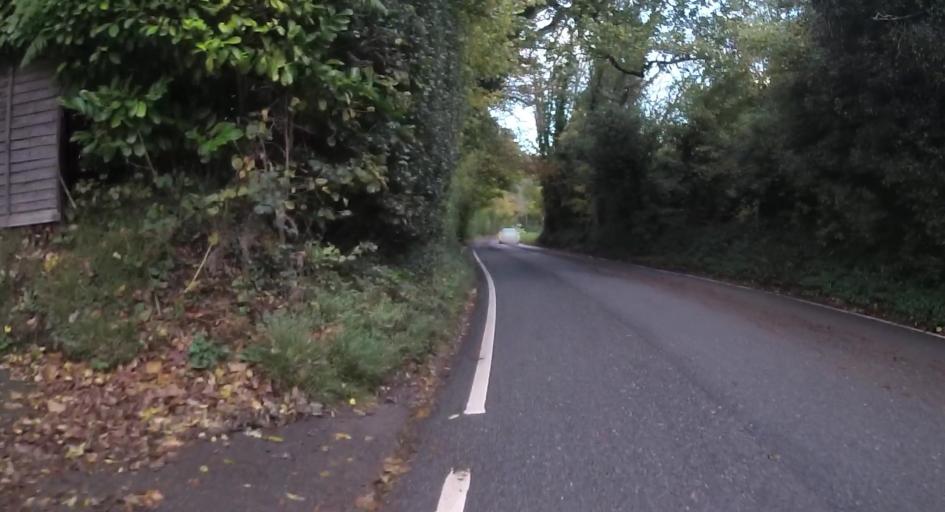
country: GB
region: England
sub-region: Hampshire
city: Alton
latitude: 51.1458
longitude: -1.0063
